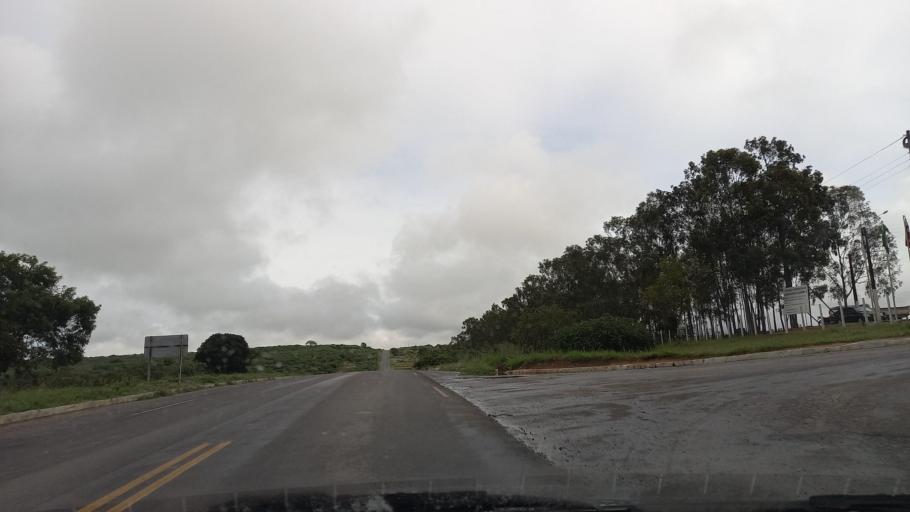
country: BR
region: Pernambuco
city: Garanhuns
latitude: -8.8407
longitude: -36.5320
